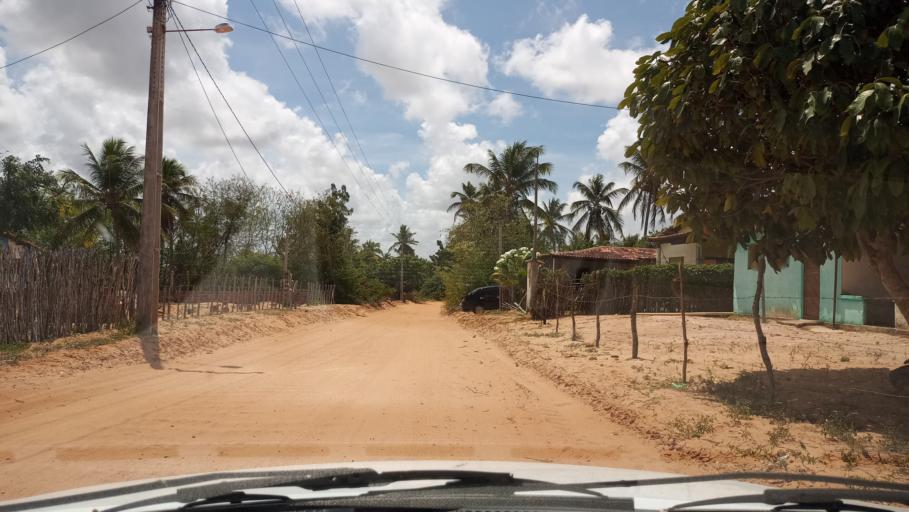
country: BR
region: Rio Grande do Norte
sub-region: Maxaranguape
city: Sao Miguel
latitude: -5.4835
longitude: -35.3297
